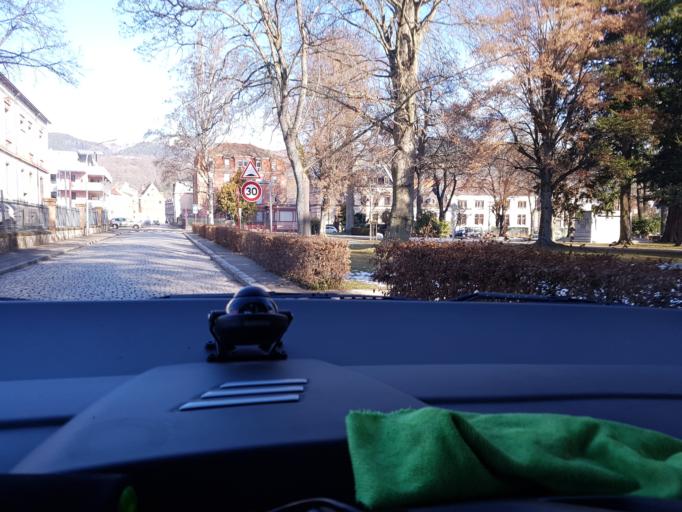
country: FR
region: Alsace
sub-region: Departement du Haut-Rhin
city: Munster
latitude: 48.0391
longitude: 7.1326
